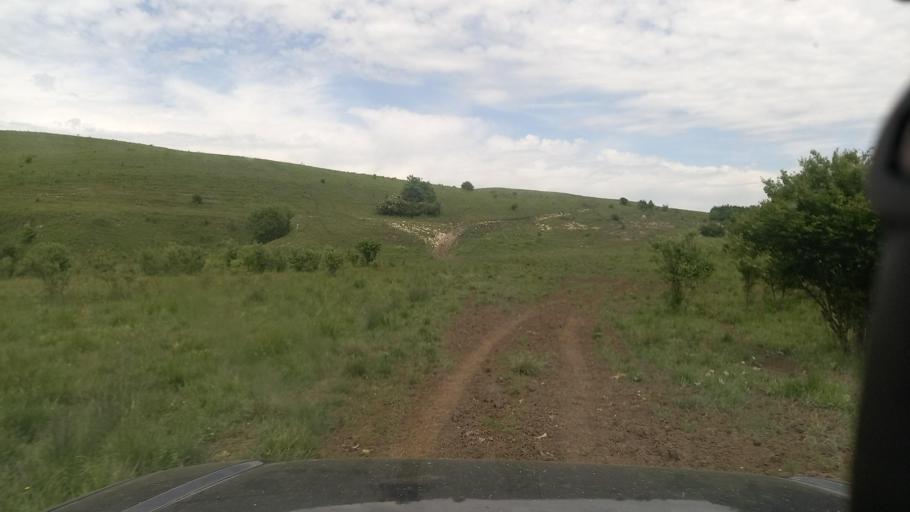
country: RU
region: Karachayevo-Cherkesiya
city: Pregradnaya
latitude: 44.0826
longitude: 41.2404
